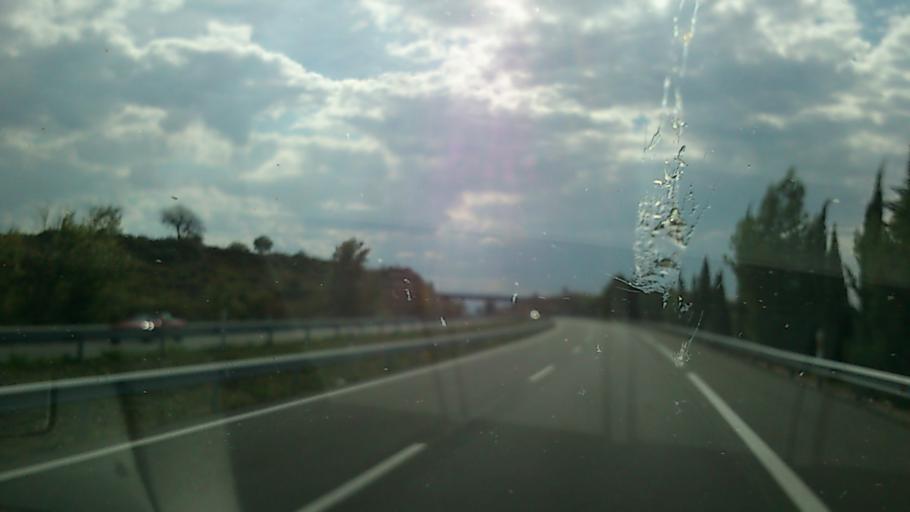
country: ES
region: La Rioja
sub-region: Provincia de La Rioja
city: Haro
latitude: 42.5919
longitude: -2.8636
